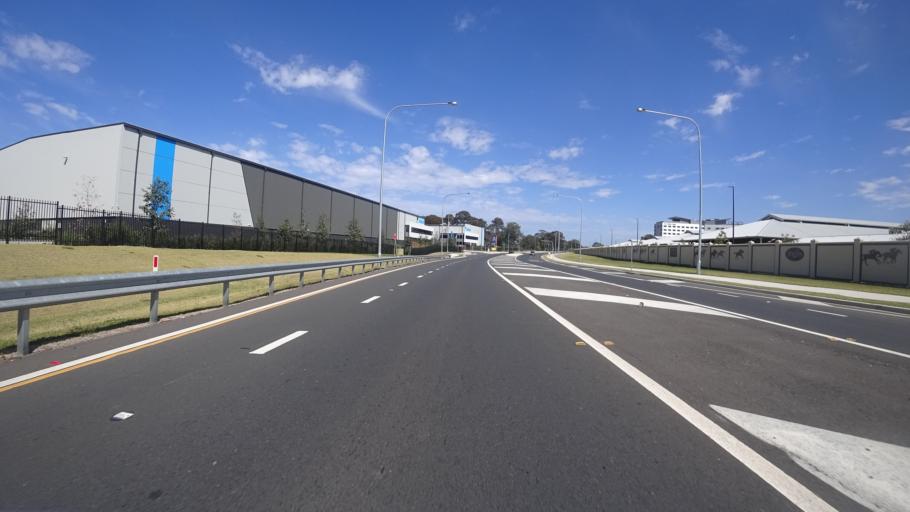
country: AU
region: New South Wales
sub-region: Fairfield
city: Chipping Norton
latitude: -33.9158
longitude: 150.9493
